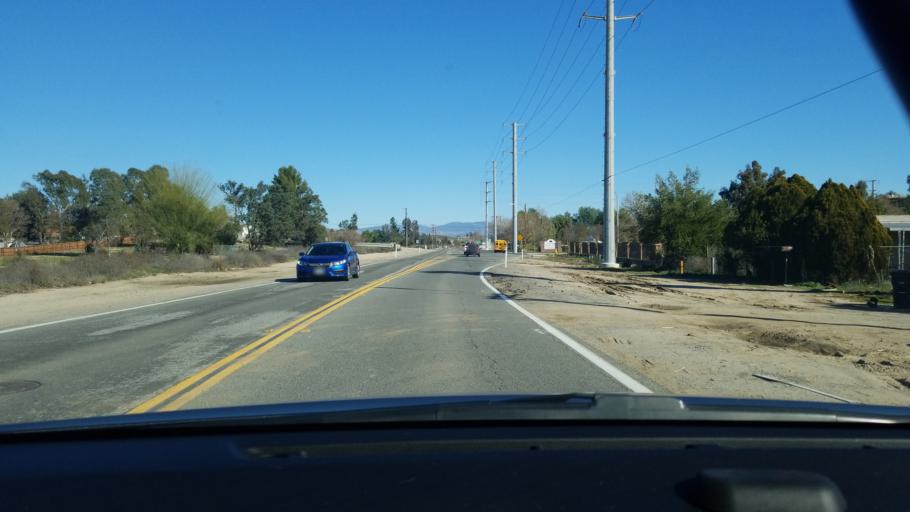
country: US
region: California
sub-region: Riverside County
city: Murrieta Hot Springs
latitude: 33.5428
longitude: -117.1184
